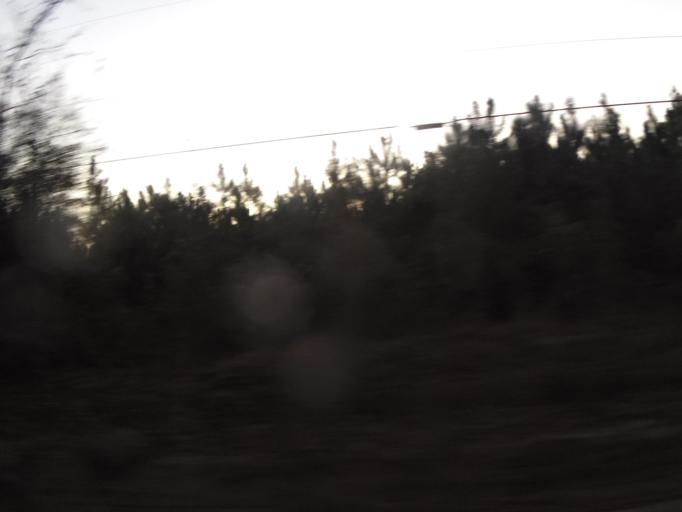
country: US
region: Florida
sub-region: Clay County
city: Asbury Lake
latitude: 29.9761
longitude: -81.7941
